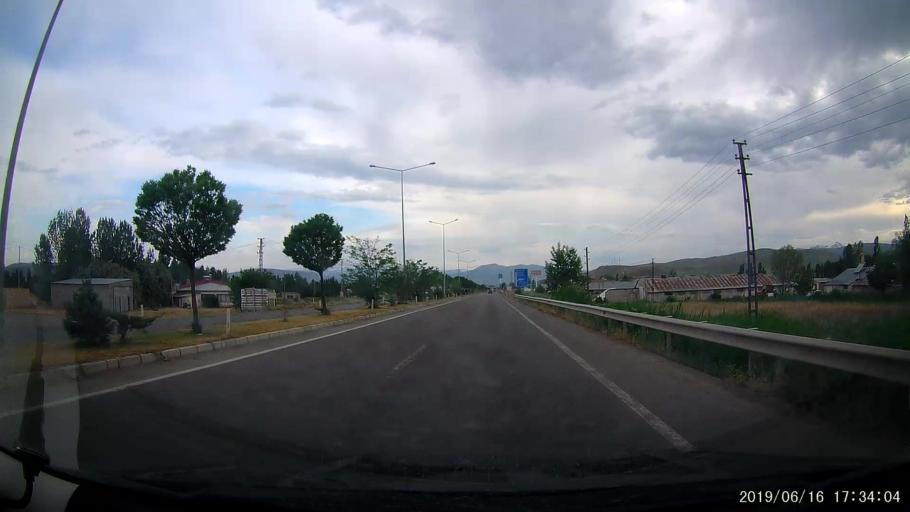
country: TR
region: Erzincan
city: Tercan
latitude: 39.7448
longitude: 40.2724
